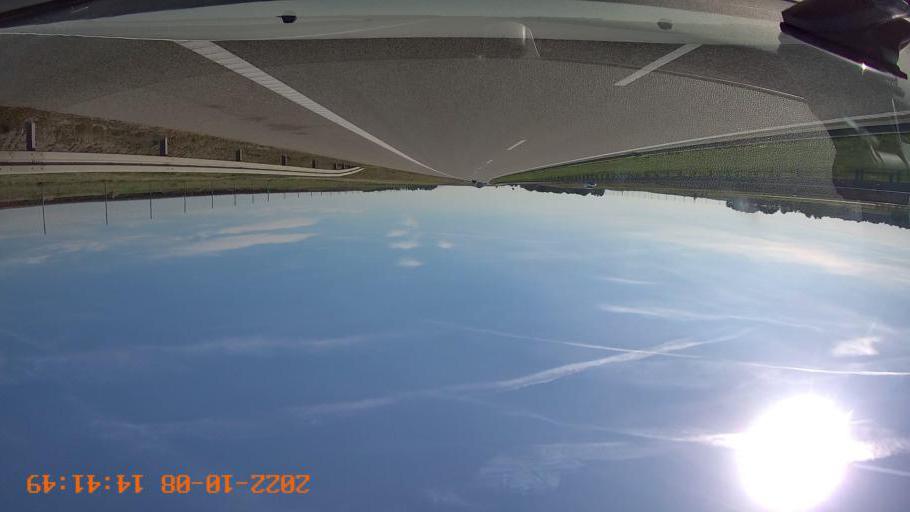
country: PL
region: Subcarpathian Voivodeship
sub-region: Powiat debicki
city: Zyrakow
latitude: 50.0898
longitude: 21.3311
